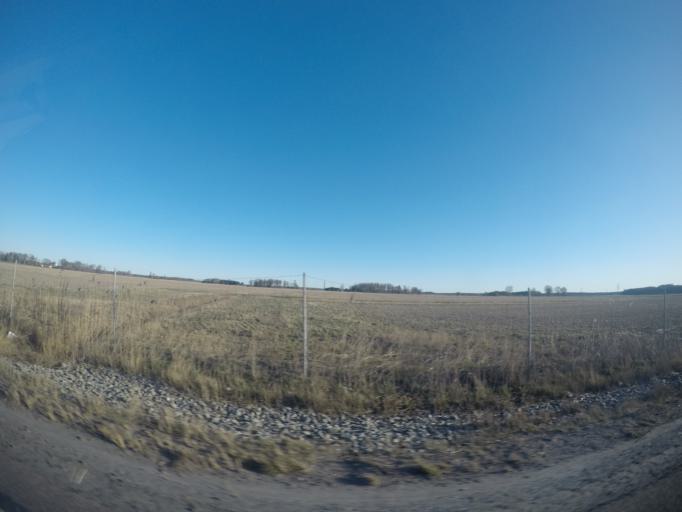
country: SE
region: Vaestmanland
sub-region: Kungsors Kommun
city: Kungsoer
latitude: 59.4099
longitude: 16.0270
